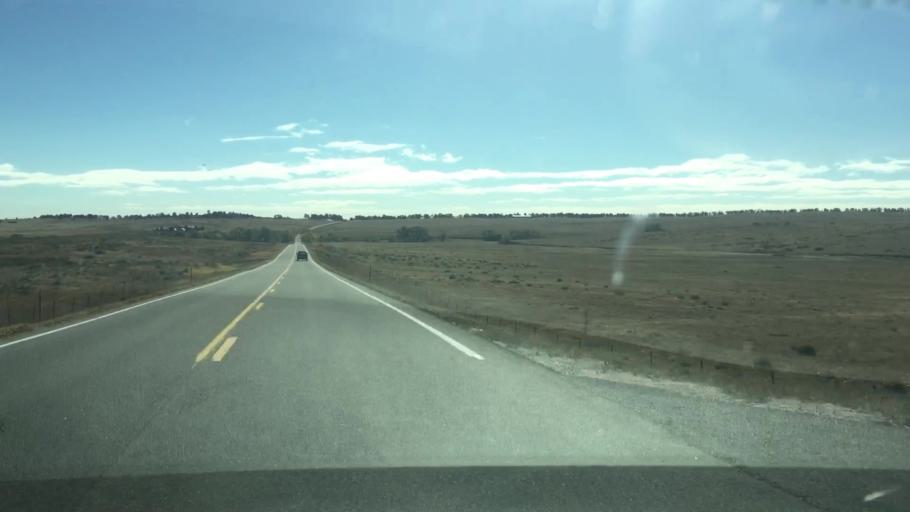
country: US
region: Colorado
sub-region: Elbert County
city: Kiowa
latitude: 39.3251
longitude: -104.3943
